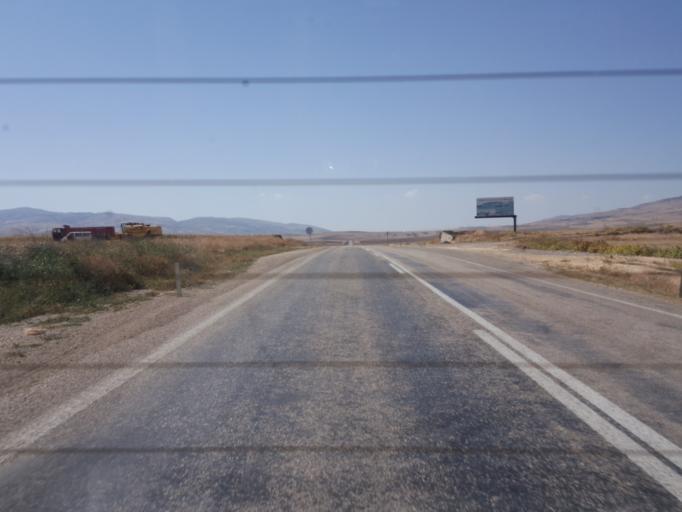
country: TR
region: Amasya
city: Dogantepe
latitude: 40.5771
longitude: 35.6158
